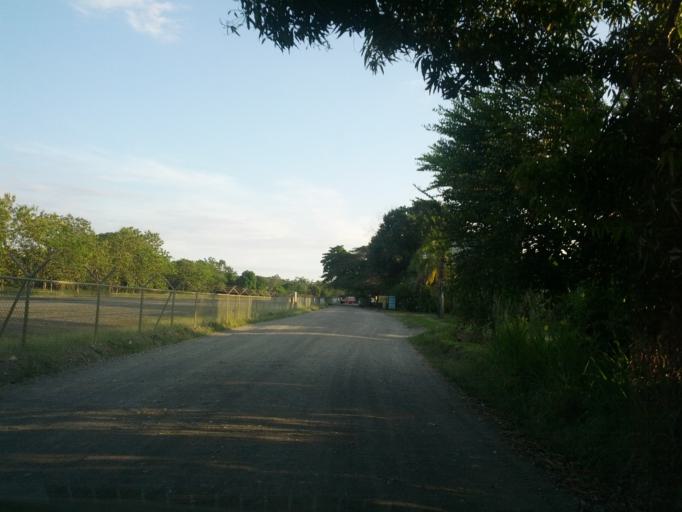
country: CR
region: Puntarenas
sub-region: Canton de Golfito
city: Golfito
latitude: 8.5374
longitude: -83.3020
